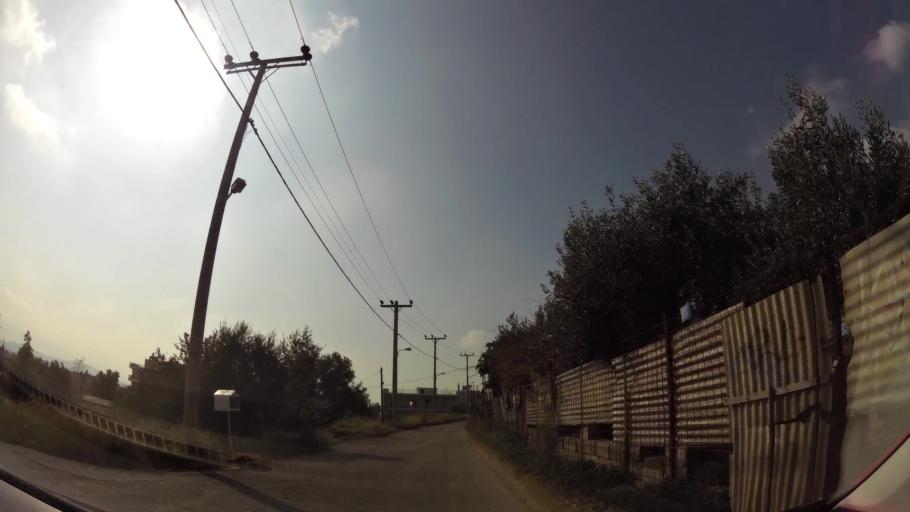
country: GR
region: Attica
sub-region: Nomarchia Dytikis Attikis
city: Zefyri
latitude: 38.0591
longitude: 23.7278
